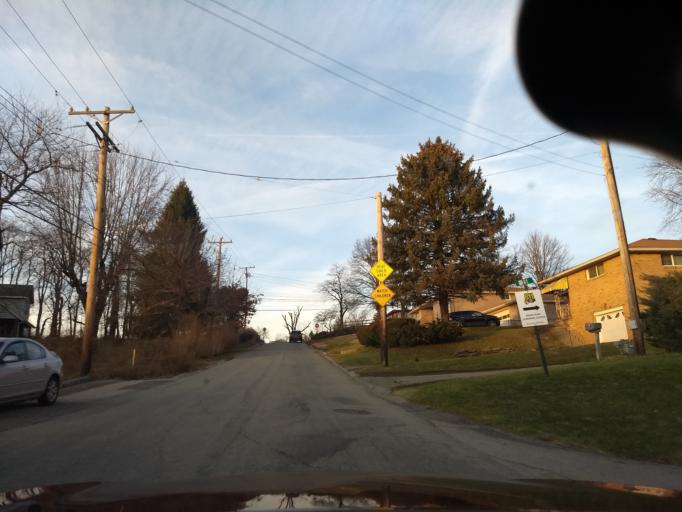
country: US
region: Pennsylvania
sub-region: Allegheny County
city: West Homestead
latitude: 40.3621
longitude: -79.9270
